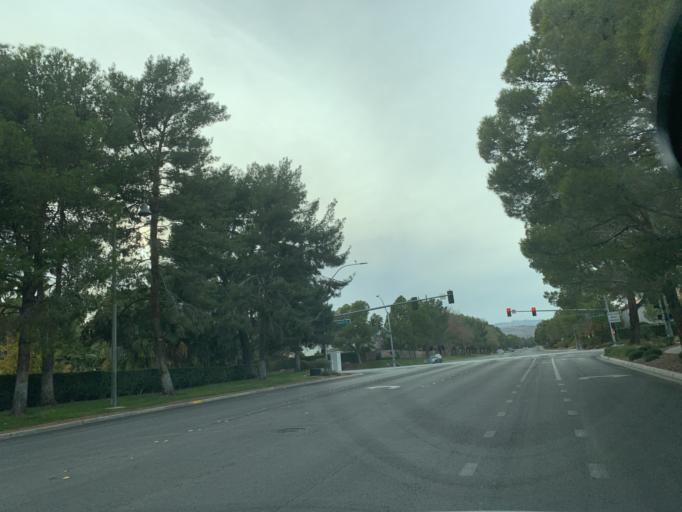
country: US
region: Nevada
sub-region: Clark County
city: Summerlin South
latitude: 36.1408
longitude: -115.2968
